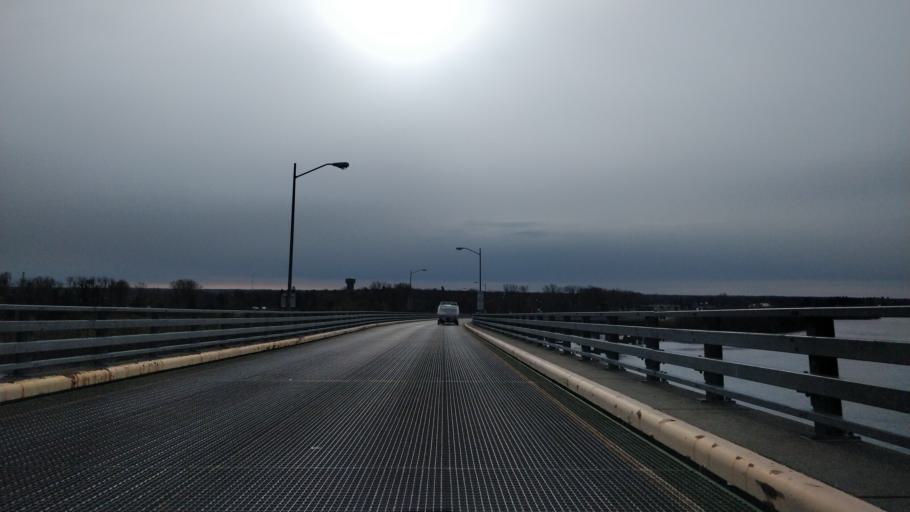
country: US
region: New York
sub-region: St. Lawrence County
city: Ogdensburg
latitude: 44.7325
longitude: -75.4573
